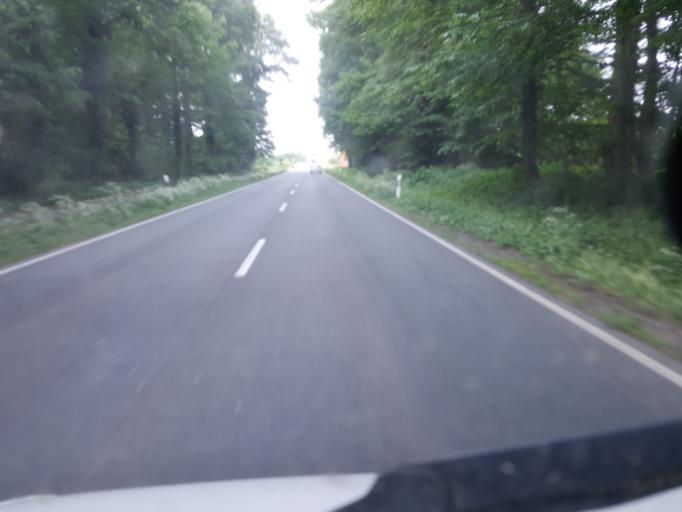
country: DE
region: Lower Saxony
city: Binnen
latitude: 52.6227
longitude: 9.1233
